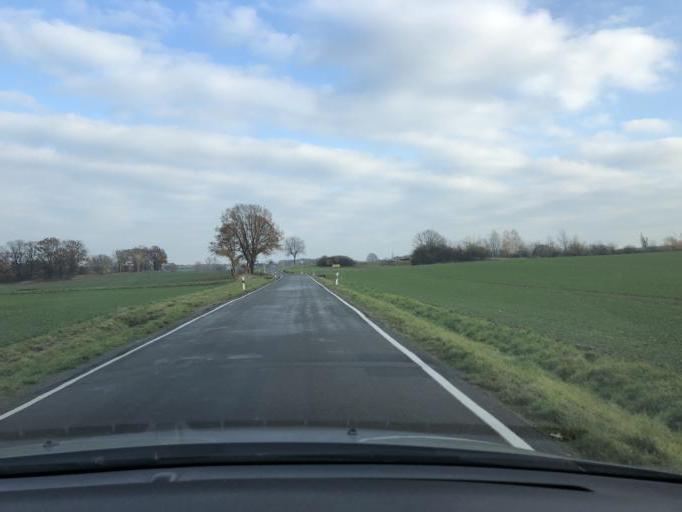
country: DE
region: Saxony
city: Nerchau
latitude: 51.2778
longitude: 12.8027
